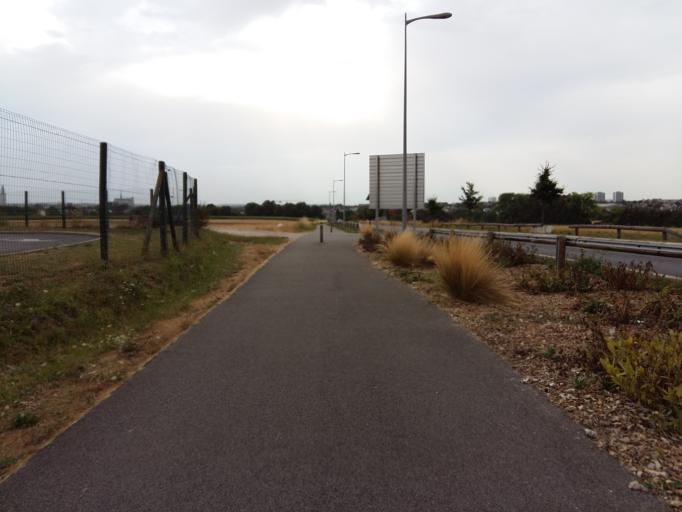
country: FR
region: Picardie
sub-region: Departement de la Somme
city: Camon
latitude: 49.9010
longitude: 2.3399
